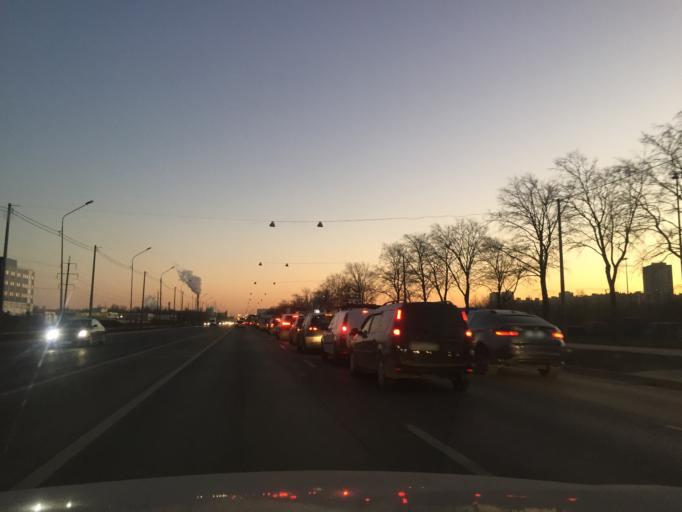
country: RU
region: St.-Petersburg
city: Obukhovo
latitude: 59.8574
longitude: 30.4220
